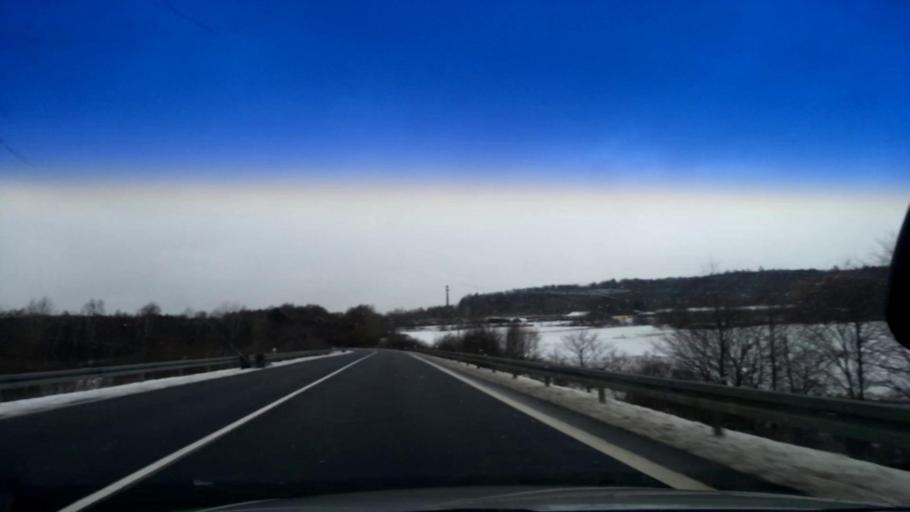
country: CZ
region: Karlovarsky
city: As
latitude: 50.2045
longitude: 12.1942
